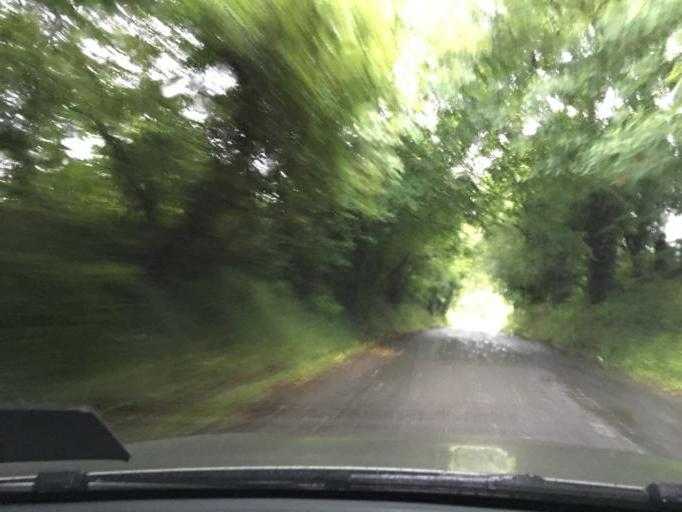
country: GB
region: Northern Ireland
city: Irvinestown
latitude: 54.5526
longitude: -7.8321
